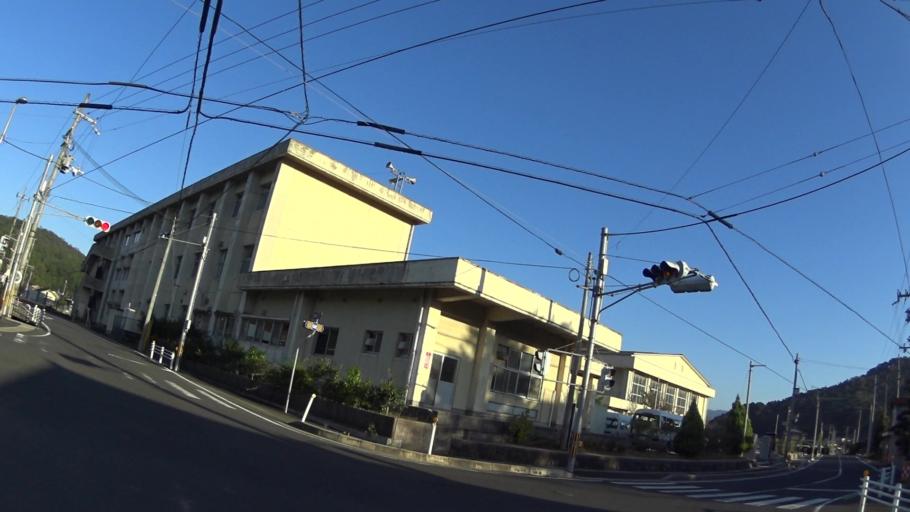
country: JP
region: Hyogo
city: Toyooka
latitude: 35.6205
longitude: 134.9453
